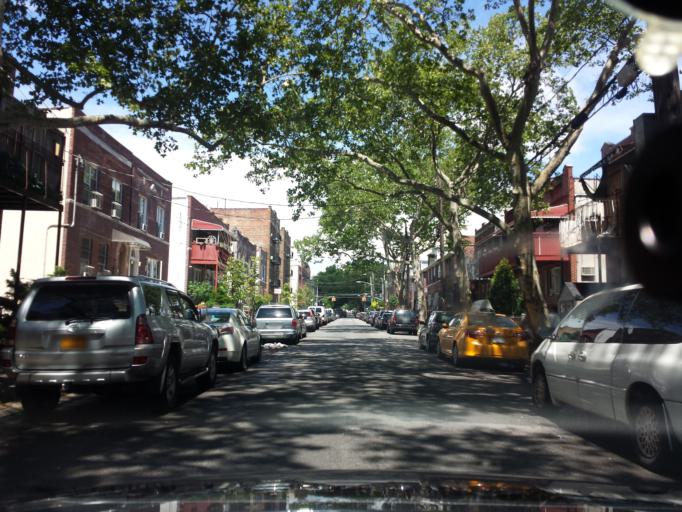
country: US
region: New York
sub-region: Kings County
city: Bensonhurst
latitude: 40.6419
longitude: -74.0005
